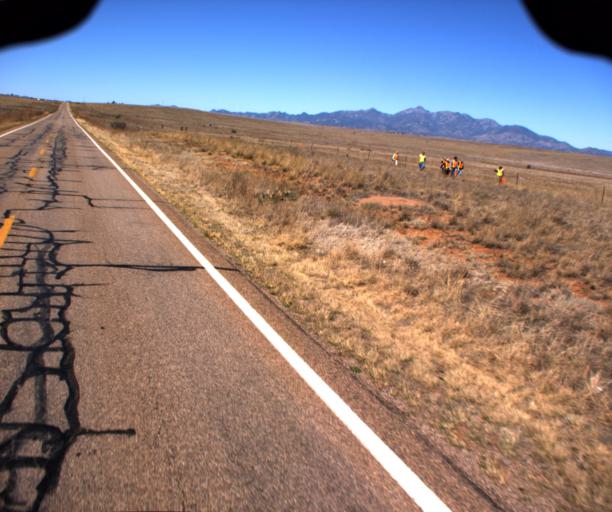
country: US
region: Arizona
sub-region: Cochise County
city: Huachuca City
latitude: 31.6982
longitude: -110.5967
